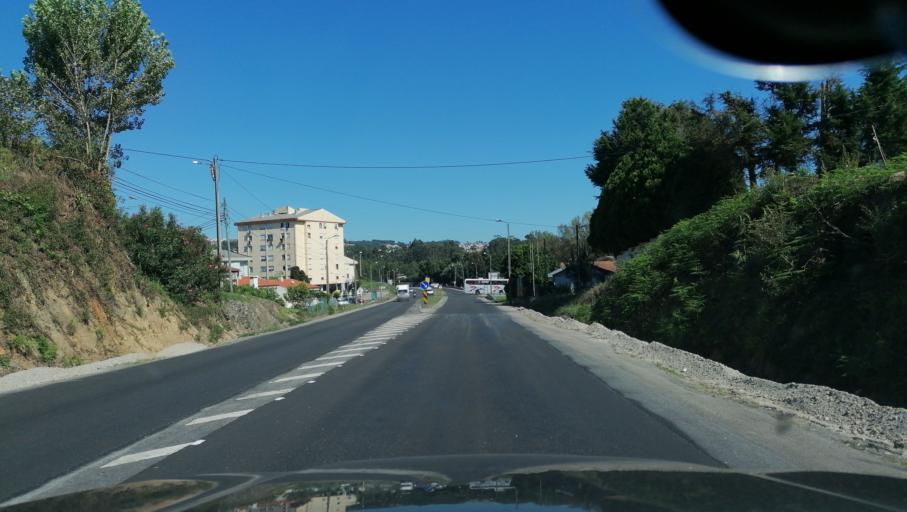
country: PT
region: Aveiro
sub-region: Santa Maria da Feira
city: Feira
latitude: 40.9321
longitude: -8.5384
